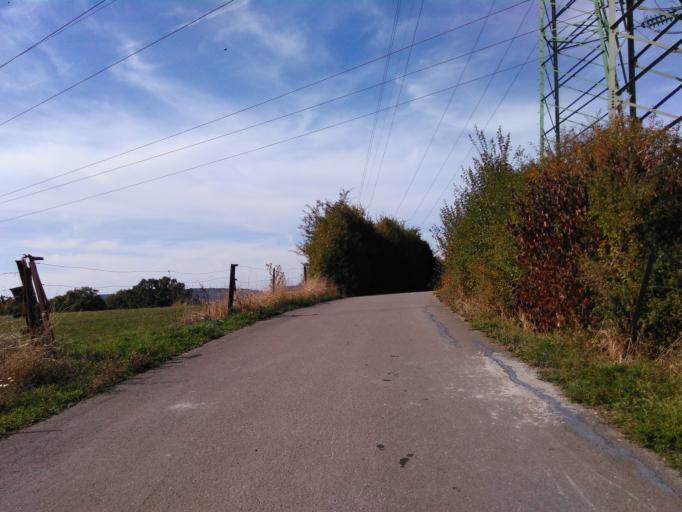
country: LU
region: Luxembourg
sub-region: Canton d'Esch-sur-Alzette
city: Sanem
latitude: 49.5525
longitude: 5.9144
